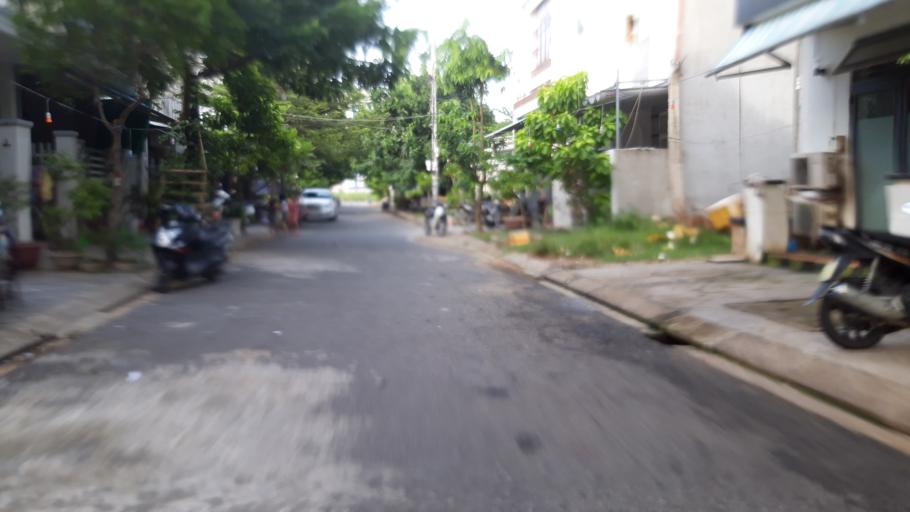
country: VN
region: Da Nang
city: Da Nang
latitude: 16.0911
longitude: 108.2278
